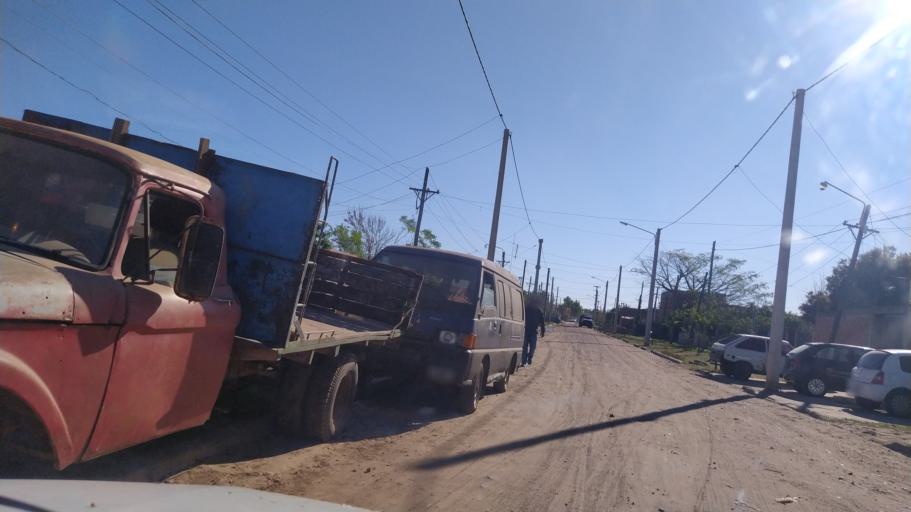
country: AR
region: Corrientes
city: Corrientes
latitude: -27.4978
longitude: -58.8066
